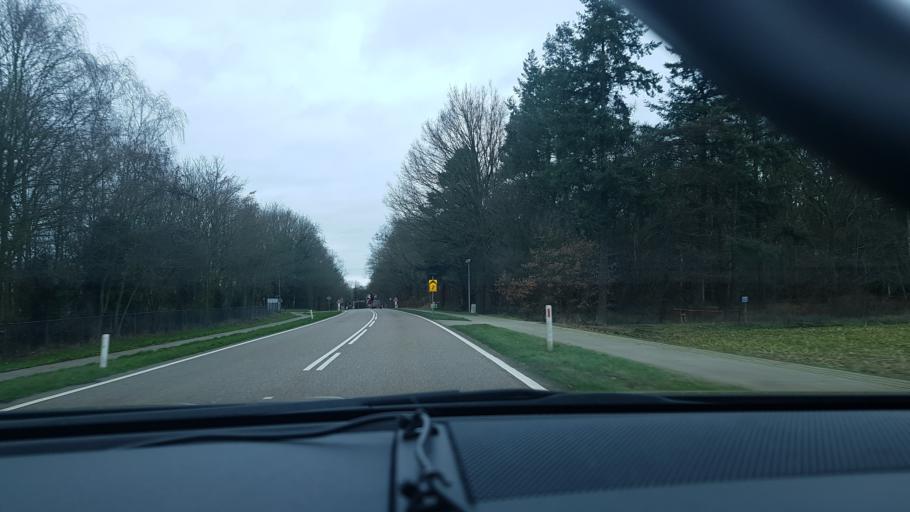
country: NL
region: Limburg
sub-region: Gemeente Leudal
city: Heythuysen
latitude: 51.2269
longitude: 5.9181
